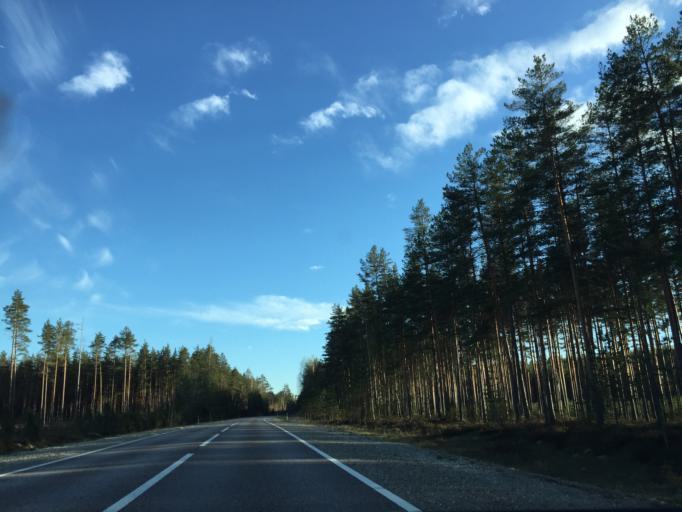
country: LV
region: Strenci
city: Seda
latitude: 57.6619
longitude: 25.8732
